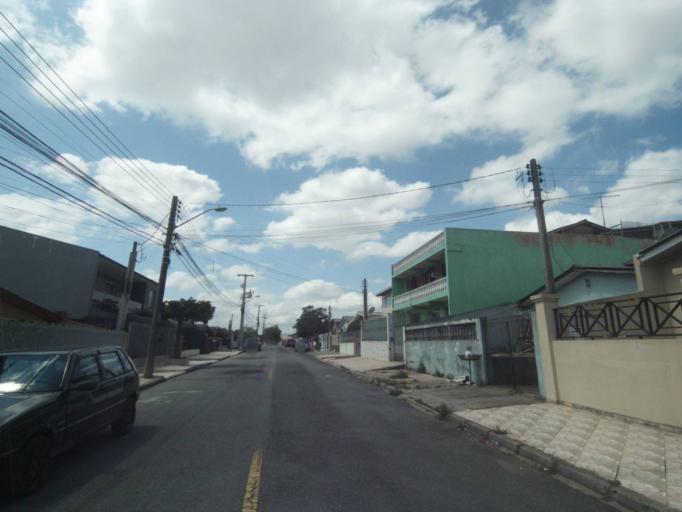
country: BR
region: Parana
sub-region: Curitiba
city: Curitiba
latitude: -25.5131
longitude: -49.3229
